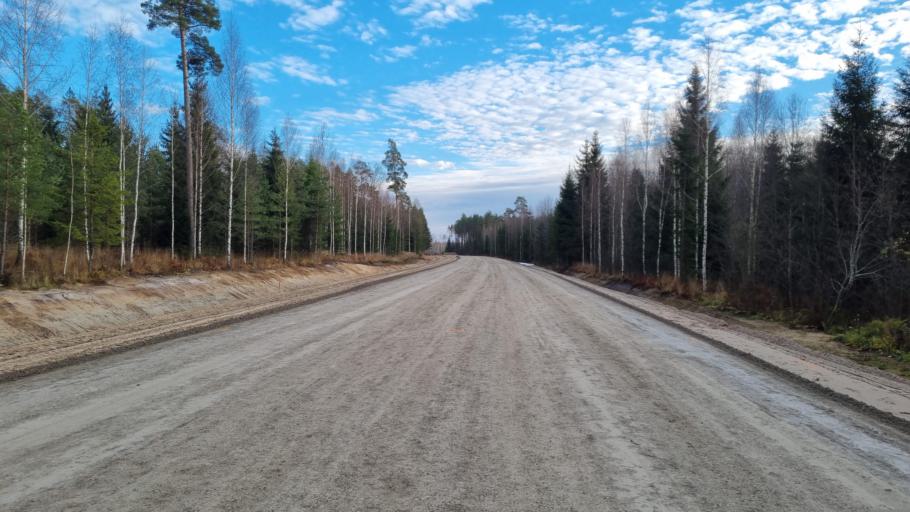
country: LV
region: Kekava
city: Kekava
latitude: 56.7911
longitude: 24.2152
